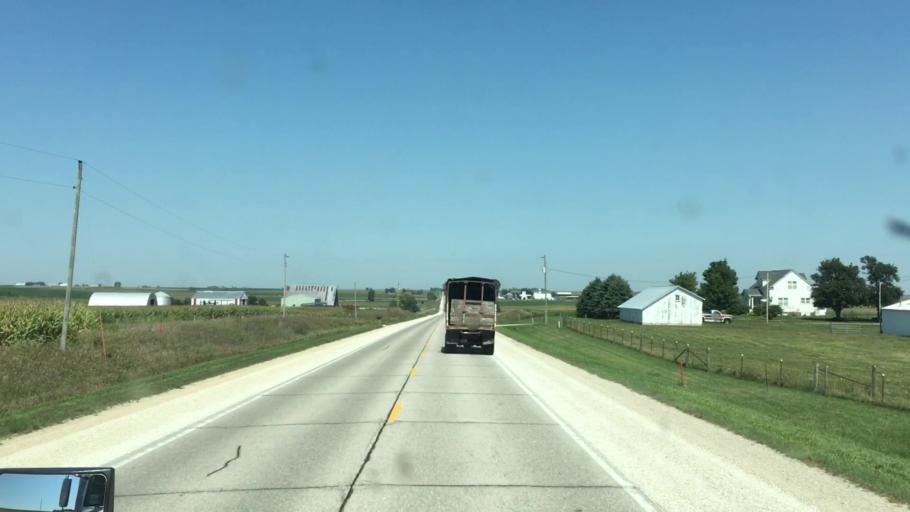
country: US
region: Iowa
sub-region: Tama County
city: Dysart
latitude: 42.0610
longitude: -92.2988
